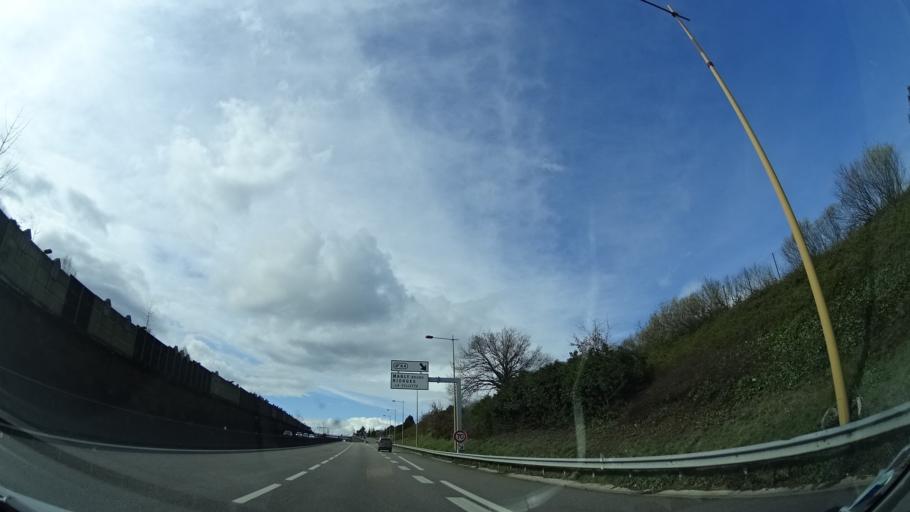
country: FR
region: Rhone-Alpes
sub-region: Departement de la Loire
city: Mably
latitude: 46.0611
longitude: 4.0670
